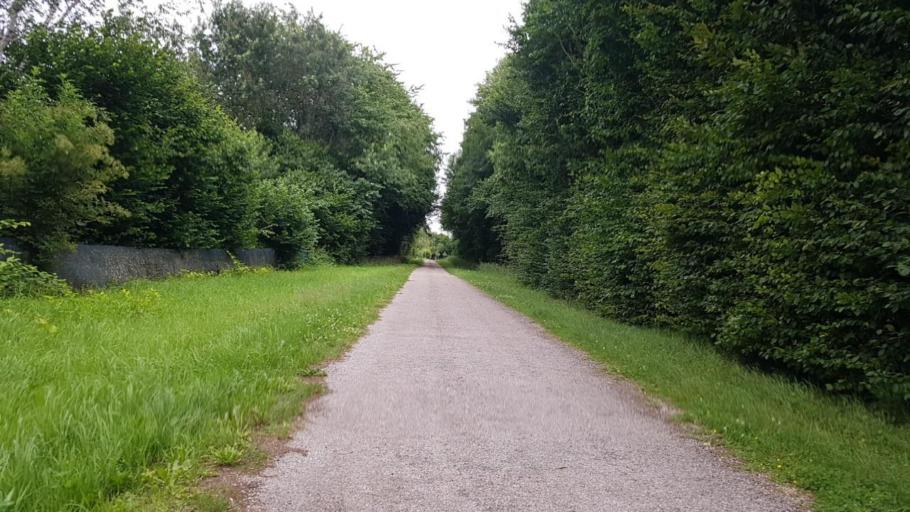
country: FR
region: Picardie
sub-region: Departement de l'Aisne
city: Origny-en-Thierache
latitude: 49.9280
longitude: 4.0321
